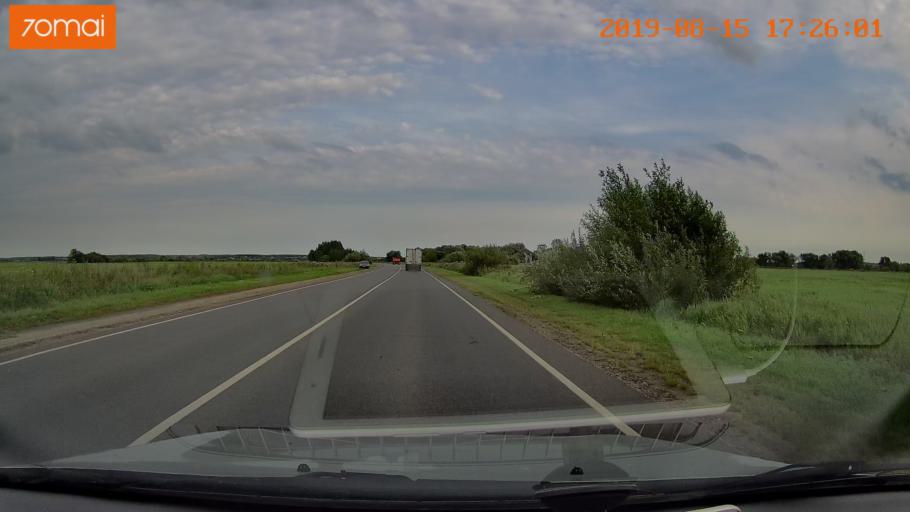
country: RU
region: Moskovskaya
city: Troitskoye
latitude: 55.3686
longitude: 38.5737
